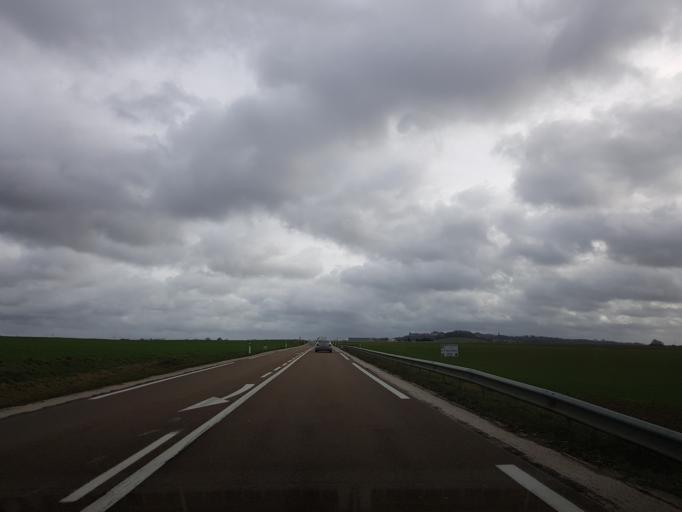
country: FR
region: Champagne-Ardenne
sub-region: Departement de la Haute-Marne
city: Langres
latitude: 47.8981
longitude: 5.3092
